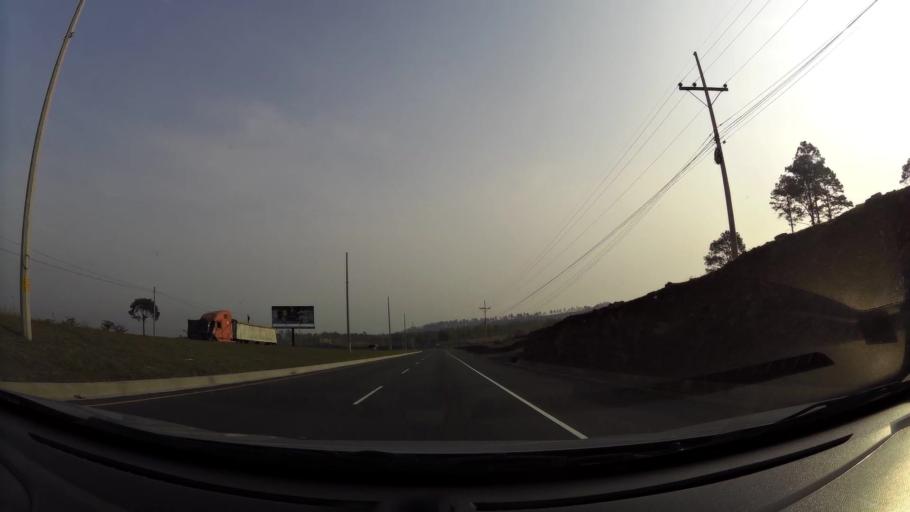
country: HN
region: Francisco Morazan
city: Tamara
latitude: 14.1797
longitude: -87.3113
